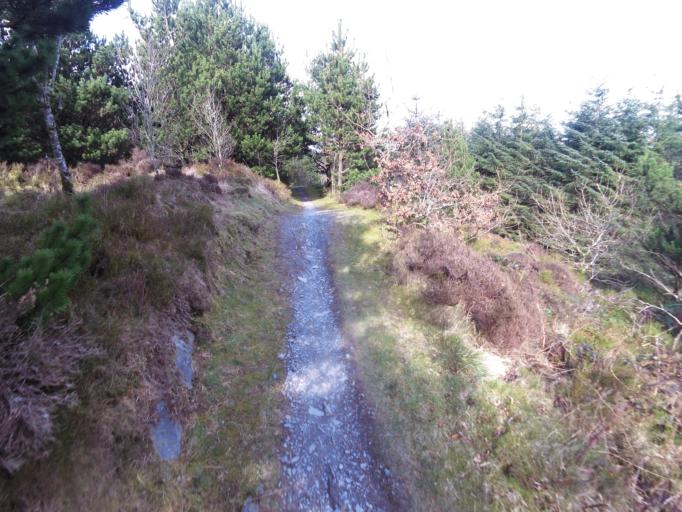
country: GB
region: Wales
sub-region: County of Ceredigion
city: Bow Street
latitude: 52.4223
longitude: -3.8832
